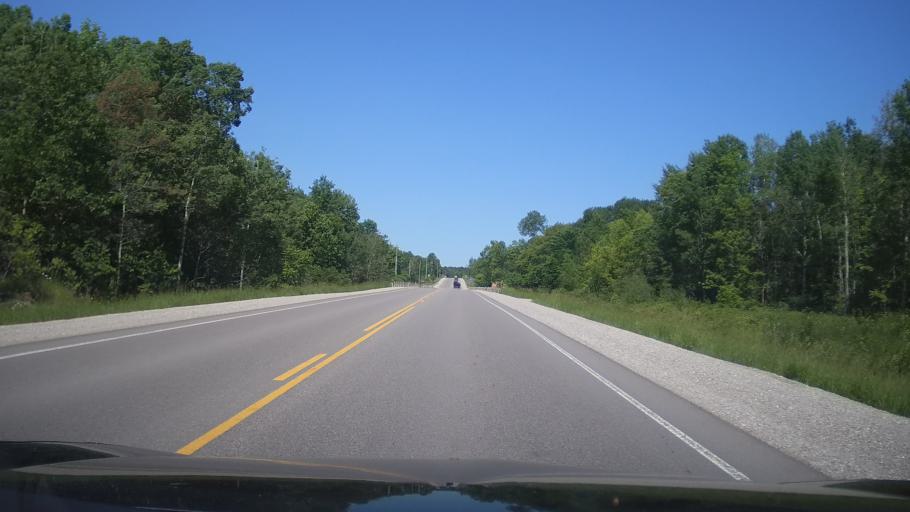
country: CA
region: Ontario
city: Orillia
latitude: 44.7418
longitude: -79.3029
